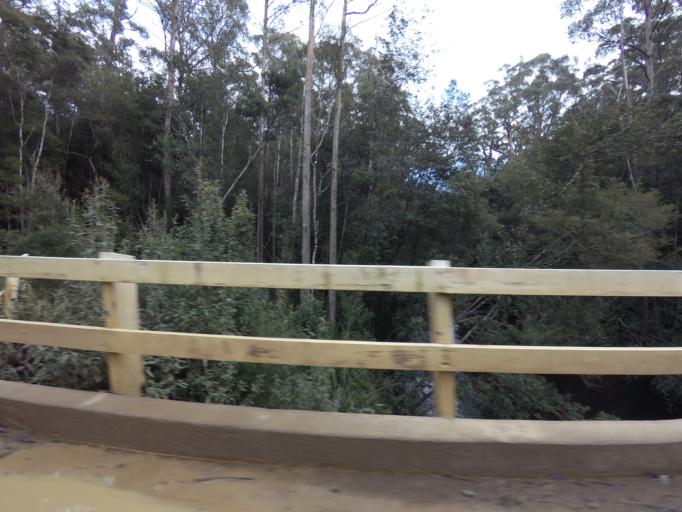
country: AU
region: Tasmania
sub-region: Huon Valley
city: Geeveston
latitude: -43.5070
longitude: 146.8758
